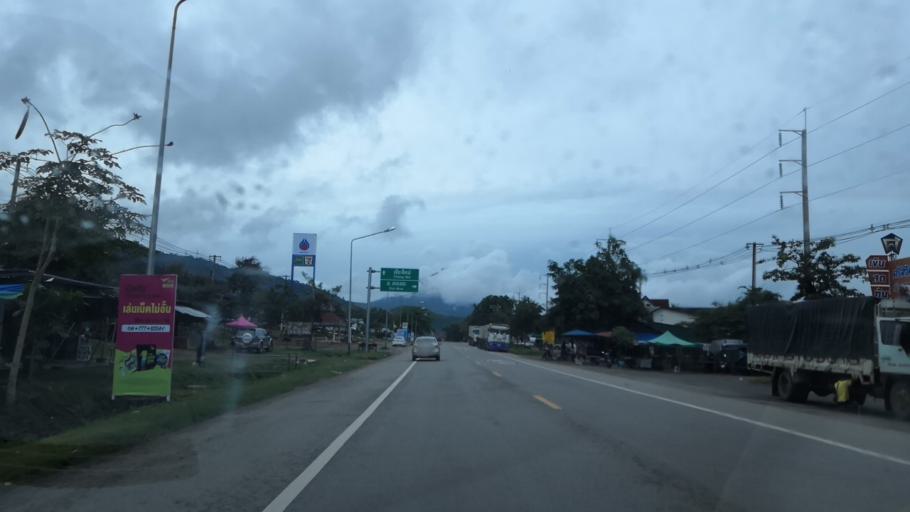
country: TH
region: Mae Hong Son
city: Ban Huai I Huak
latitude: 18.1674
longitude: 97.9355
